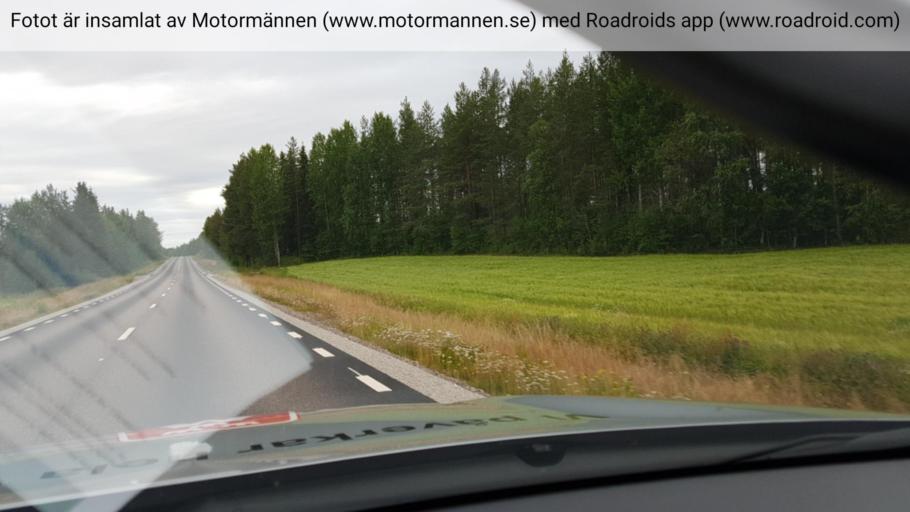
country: SE
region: Norrbotten
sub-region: Overkalix Kommun
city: OEverkalix
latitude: 66.4513
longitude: 22.7879
